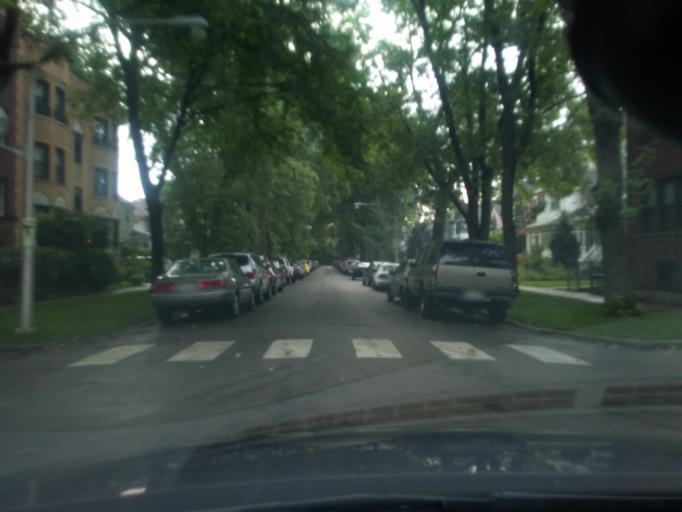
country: US
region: Illinois
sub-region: Cook County
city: Evanston
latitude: 42.0137
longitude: -87.6782
